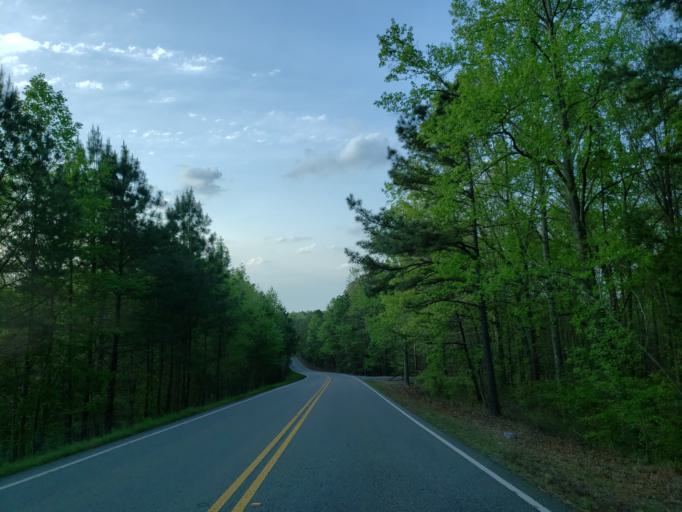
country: US
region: Georgia
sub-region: Cherokee County
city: Ball Ground
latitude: 34.2721
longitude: -84.3713
